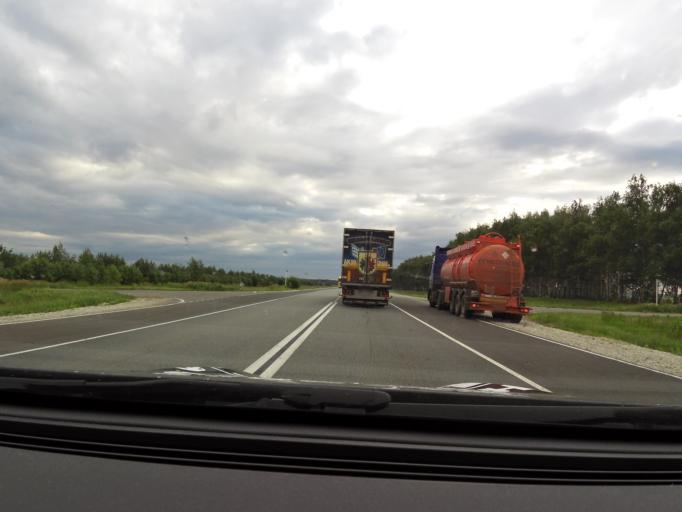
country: RU
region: Tatarstan
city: Nizhniye Vyazovyye
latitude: 55.7266
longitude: 48.4159
